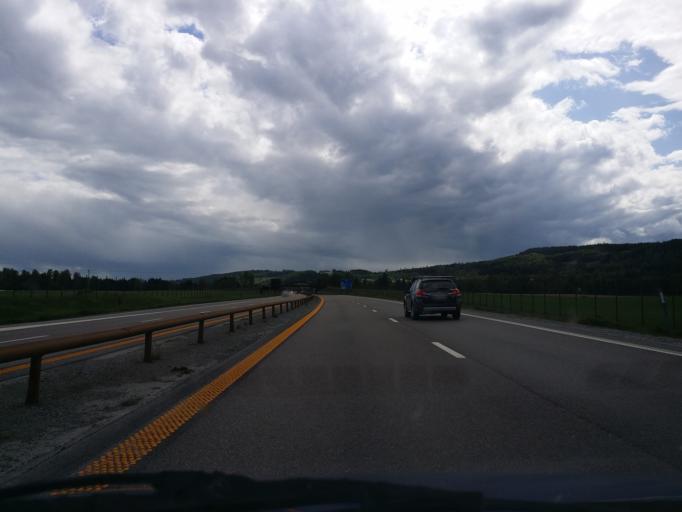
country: NO
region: Akershus
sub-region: Eidsvoll
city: Eidsvoll
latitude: 60.3856
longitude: 11.2125
